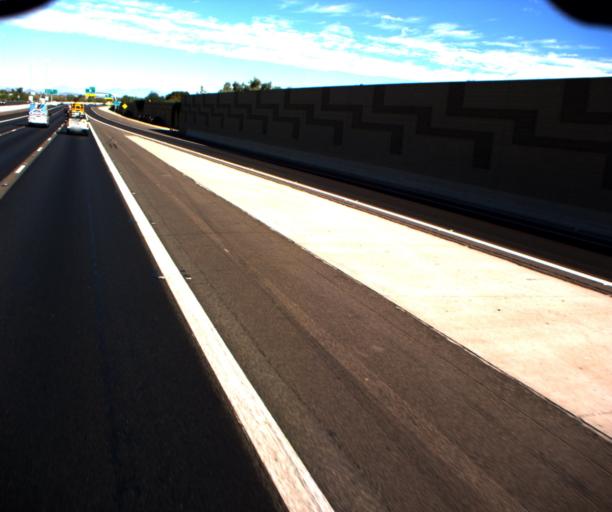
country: US
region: Arizona
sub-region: Maricopa County
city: Sun City
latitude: 33.5838
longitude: -112.2599
